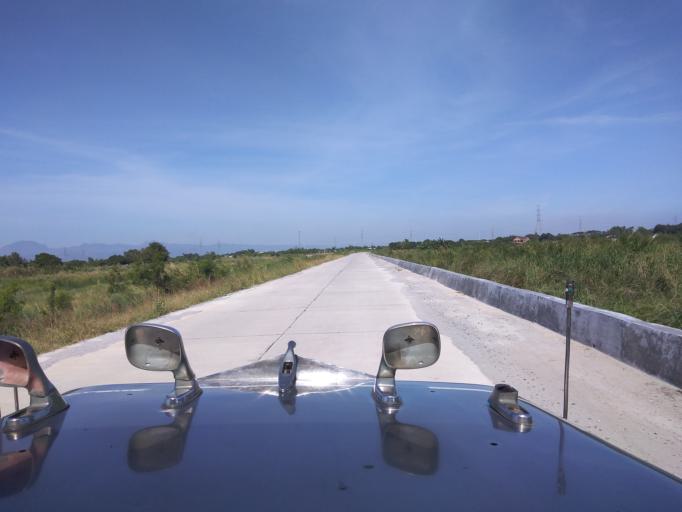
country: PH
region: Central Luzon
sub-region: Province of Pampanga
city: Bacolor
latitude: 14.9986
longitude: 120.6638
